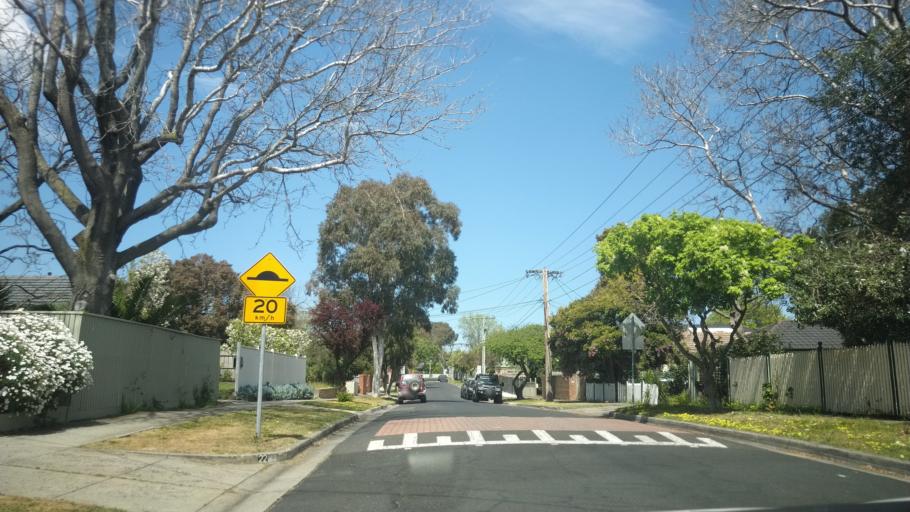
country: AU
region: Victoria
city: Highett
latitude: -37.9576
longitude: 145.0464
